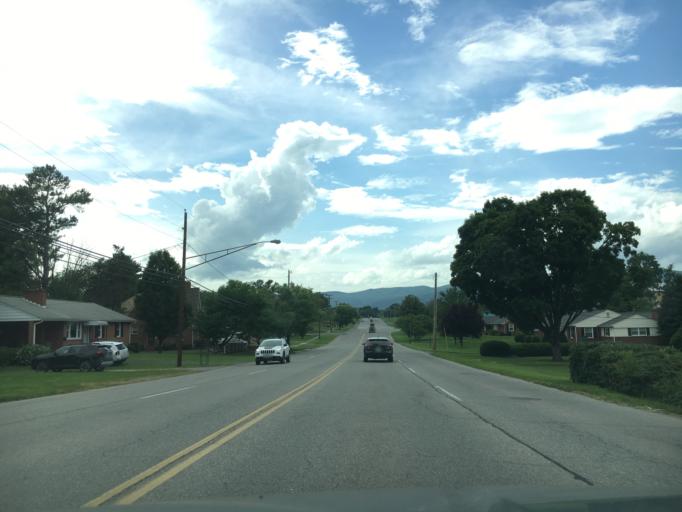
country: US
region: Virginia
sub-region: City of Salem
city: Salem
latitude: 37.2813
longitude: -80.0376
